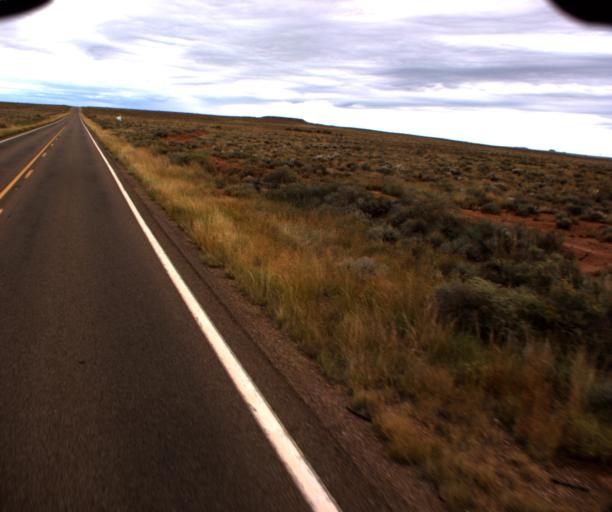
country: US
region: Arizona
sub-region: Navajo County
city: Holbrook
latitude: 34.7596
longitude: -110.1245
